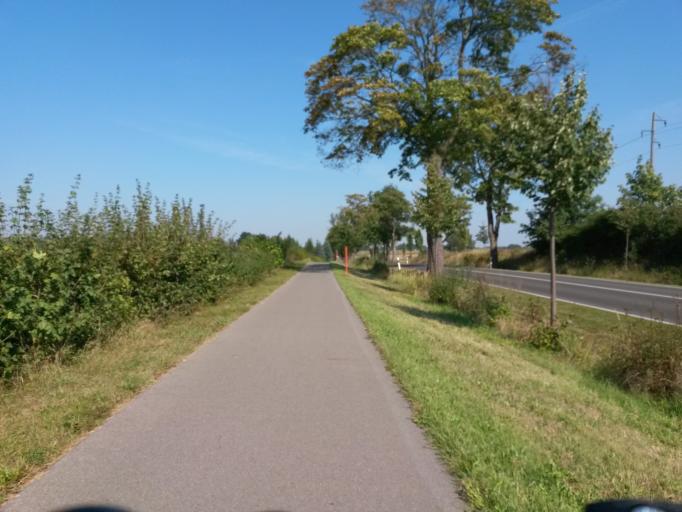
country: DE
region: Brandenburg
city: Templin
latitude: 53.0809
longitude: 13.4446
